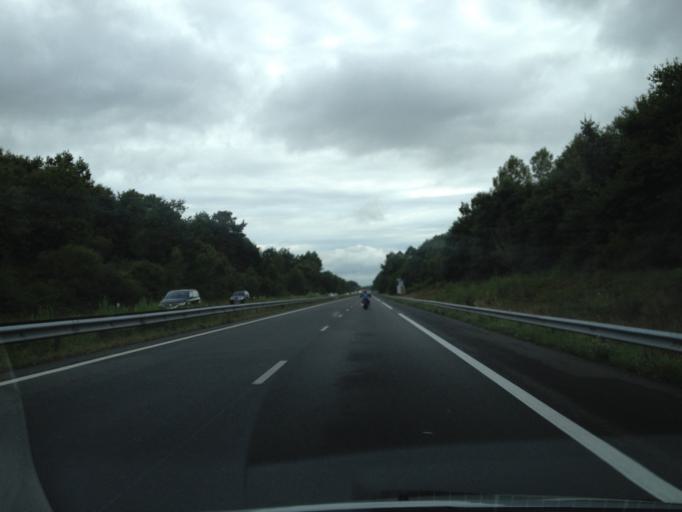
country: FR
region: Aquitaine
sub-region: Departement du Lot-et-Garonne
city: Fourques-sur-Garonne
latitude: 44.3932
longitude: 0.1949
